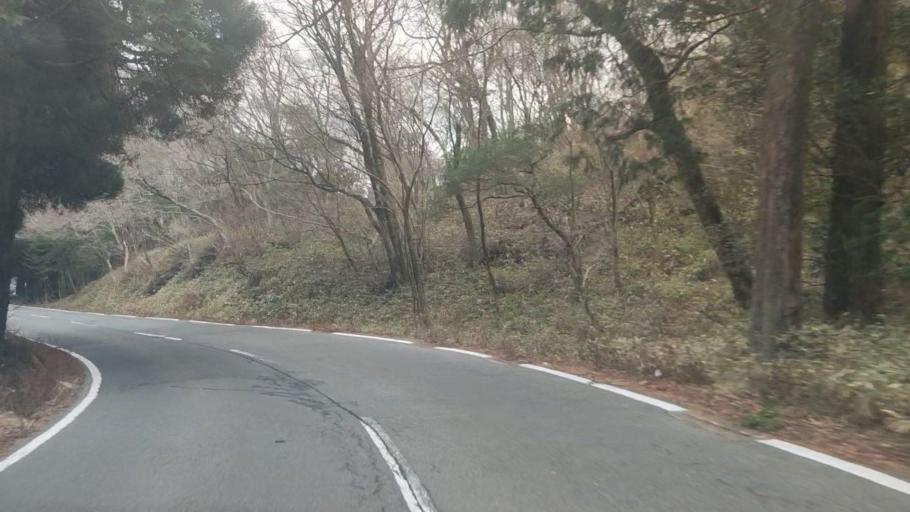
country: JP
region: Nagasaki
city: Shimabara
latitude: 32.7535
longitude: 130.2737
